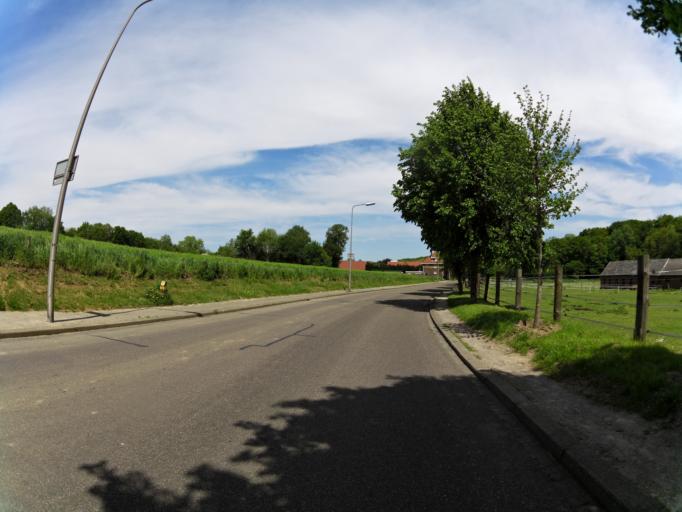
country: NL
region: Limburg
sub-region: Gemeente Kerkrade
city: Kerkrade
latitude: 50.8619
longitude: 6.0517
